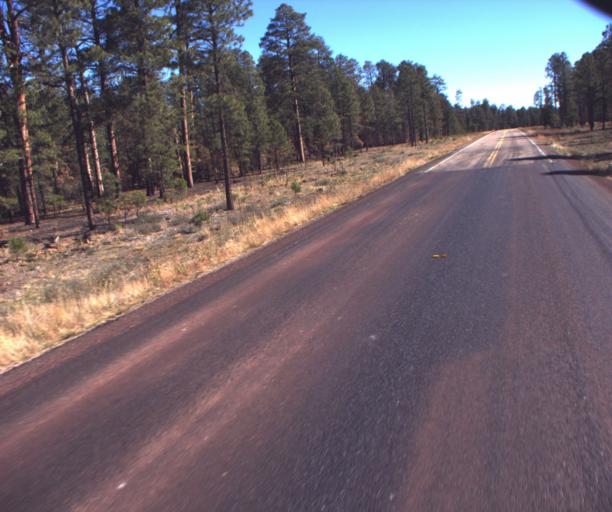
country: US
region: Arizona
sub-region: Coconino County
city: Fredonia
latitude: 36.7479
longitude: -112.2556
